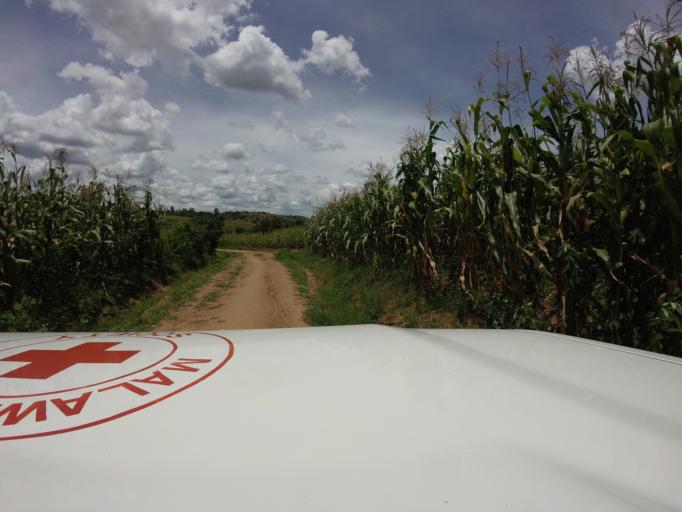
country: MW
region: Southern Region
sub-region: Thyolo District
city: Thyolo
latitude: -15.9586
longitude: 35.1657
